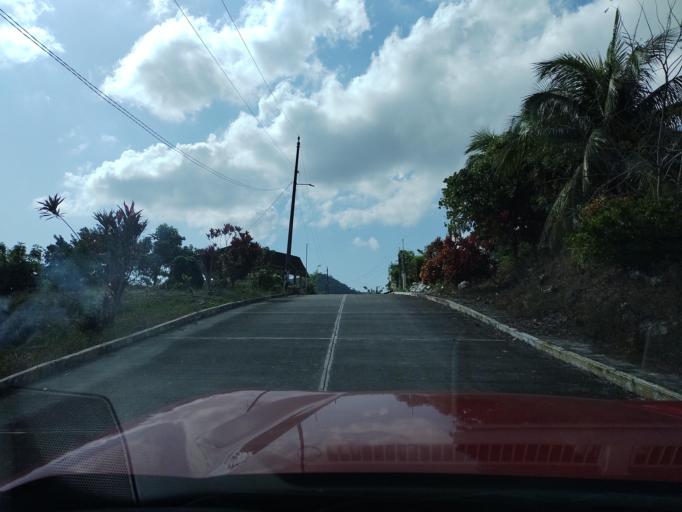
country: MX
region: Veracruz
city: Agua Dulce
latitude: 20.3056
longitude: -97.1738
